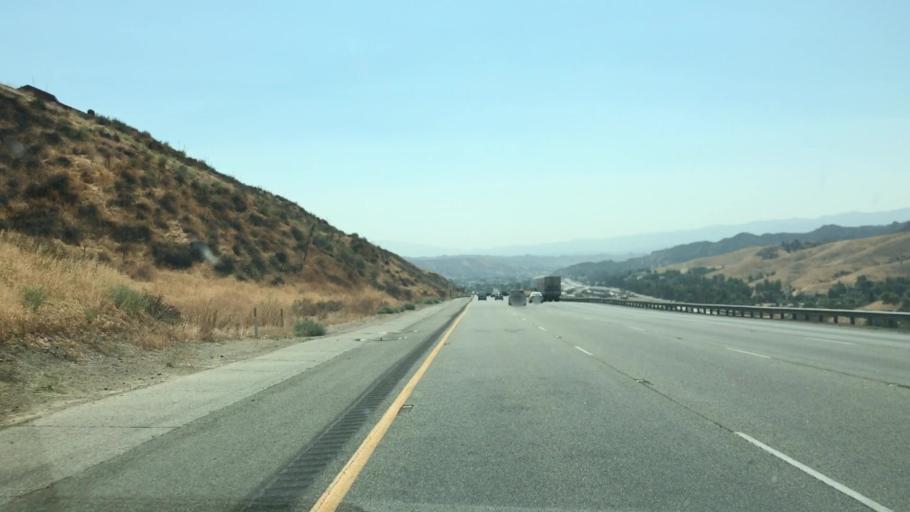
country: US
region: California
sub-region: Los Angeles County
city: Castaic
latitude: 34.5171
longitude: -118.6363
